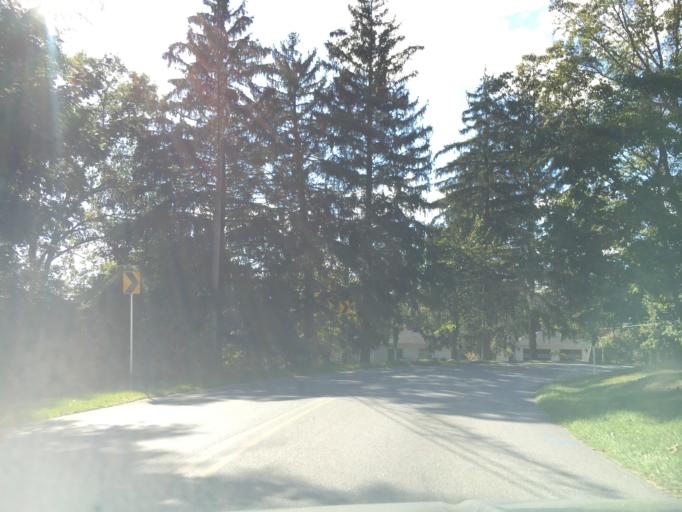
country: US
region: Pennsylvania
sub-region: York County
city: East York
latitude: 40.0040
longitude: -76.6774
